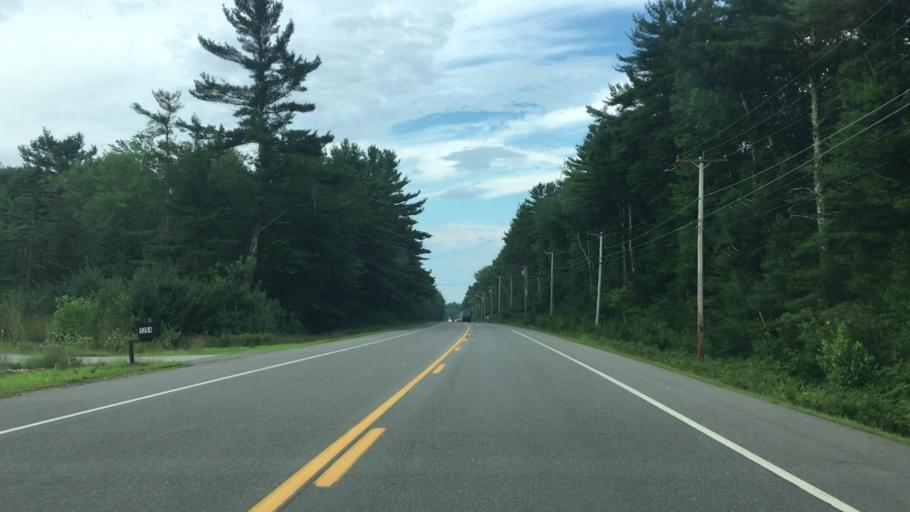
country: US
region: Maine
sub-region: York County
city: Lebanon
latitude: 43.3617
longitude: -70.9125
